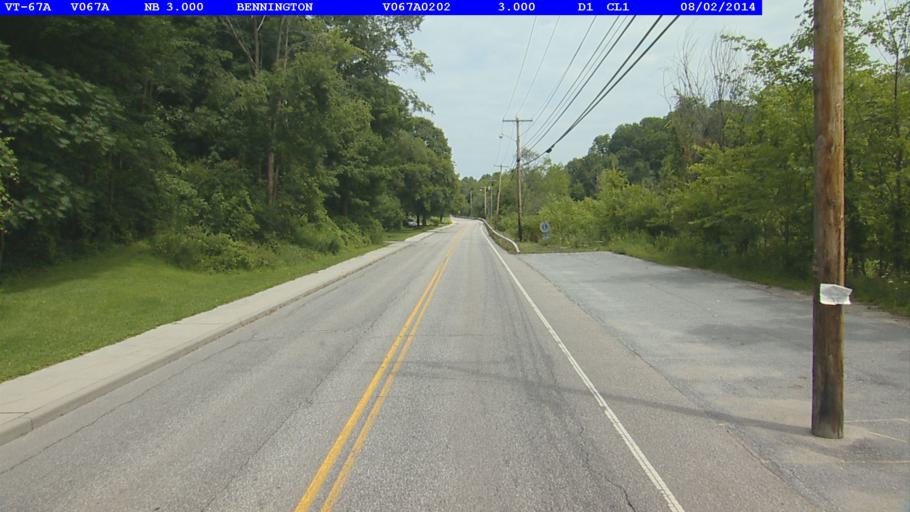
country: US
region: Vermont
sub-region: Bennington County
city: North Bennington
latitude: 42.9256
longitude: -73.2443
